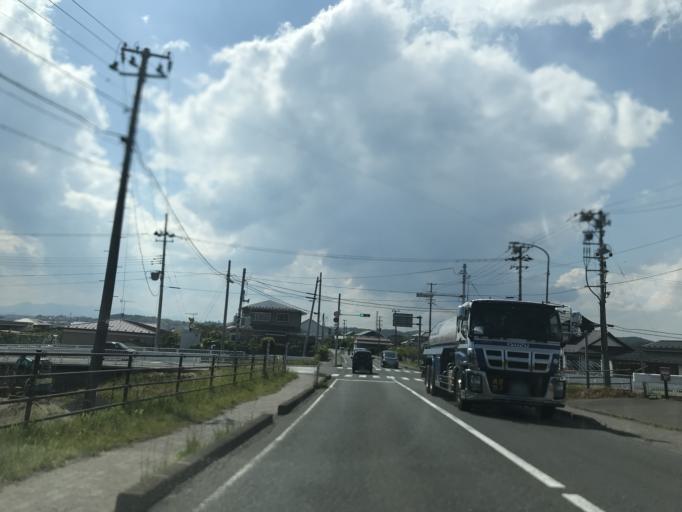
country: JP
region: Miyagi
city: Wakuya
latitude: 38.4732
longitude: 141.1236
